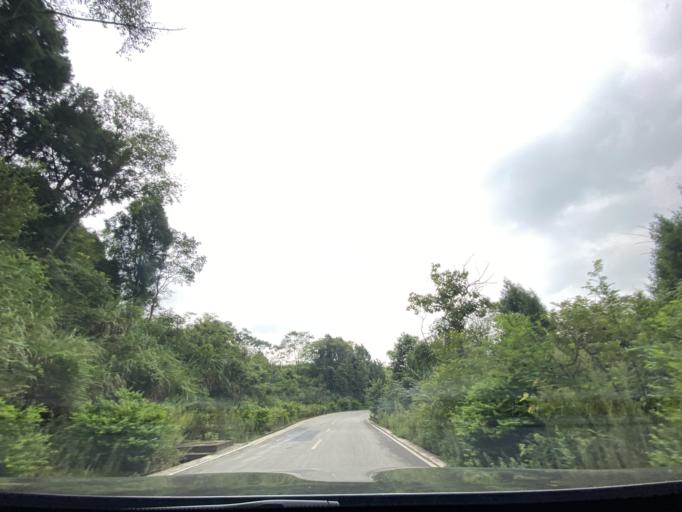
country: CN
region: Sichuan
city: Jiancheng
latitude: 30.5352
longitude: 104.5329
